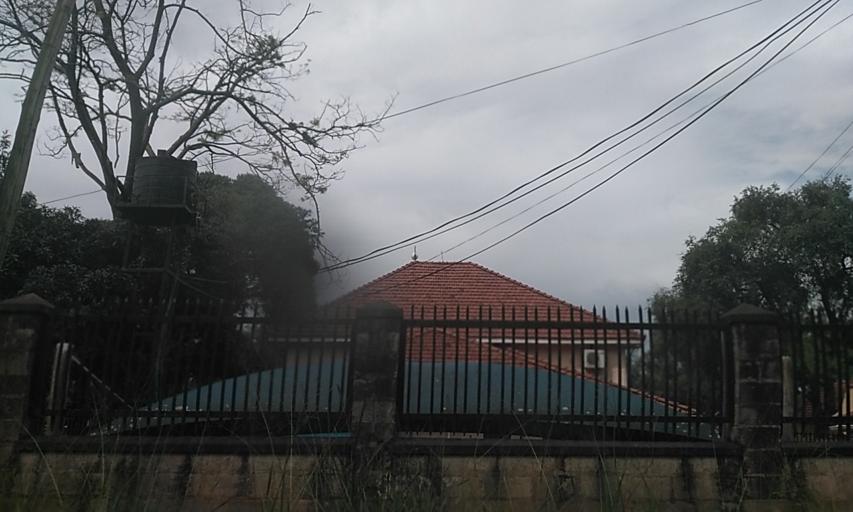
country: UG
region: Central Region
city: Kampala Central Division
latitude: 0.3311
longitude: 32.5878
